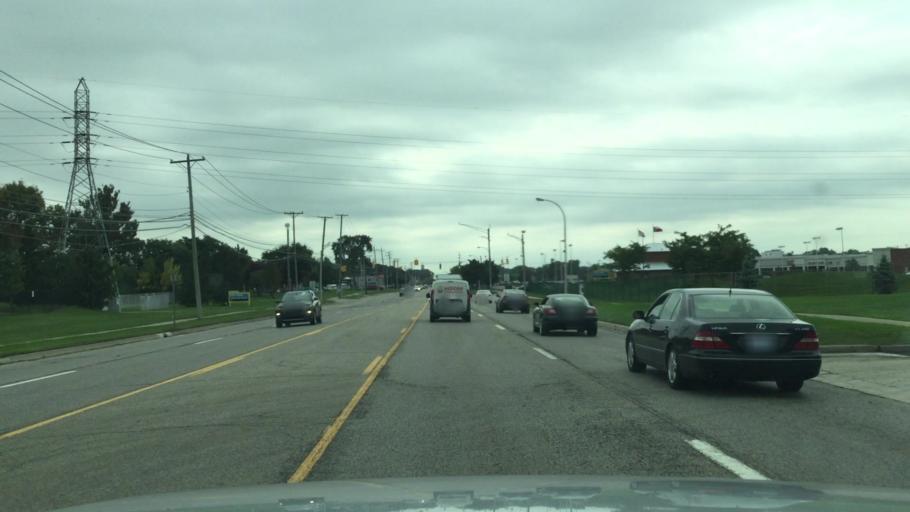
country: US
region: Michigan
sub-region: Oakland County
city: Madison Heights
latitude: 42.5103
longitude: -83.1060
